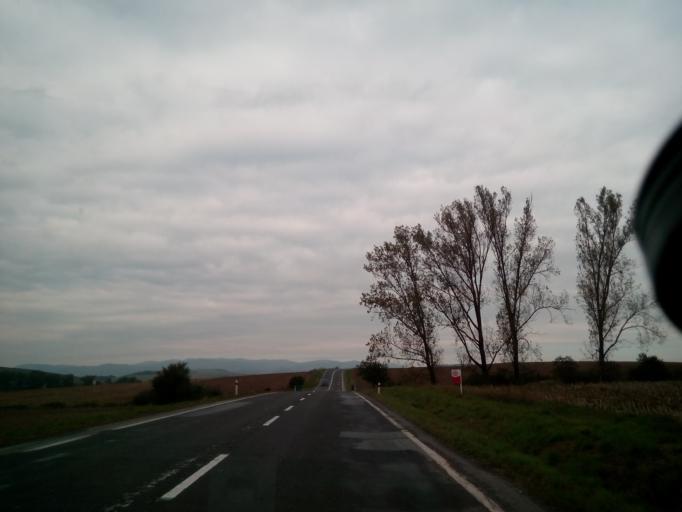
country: SK
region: Presovsky
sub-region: Okres Presov
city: Presov
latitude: 49.0795
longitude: 21.3199
